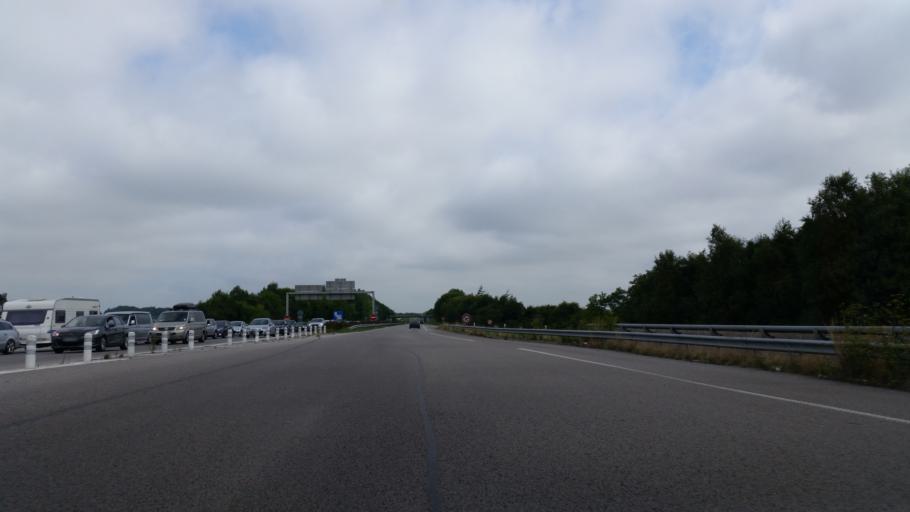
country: FR
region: Haute-Normandie
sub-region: Departement de la Seine-Maritime
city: Etainhus
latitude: 49.5540
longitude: 0.3366
